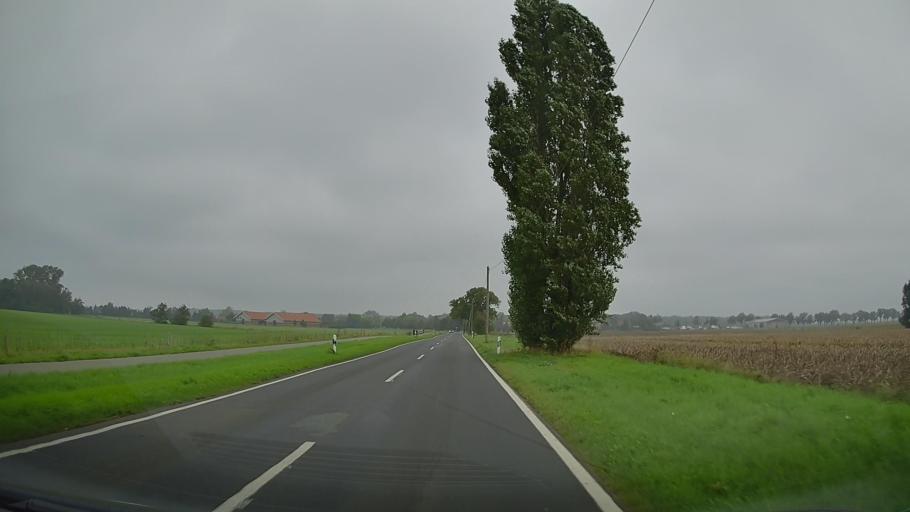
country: DE
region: Mecklenburg-Vorpommern
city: Neubukow
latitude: 54.0687
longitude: 11.6295
